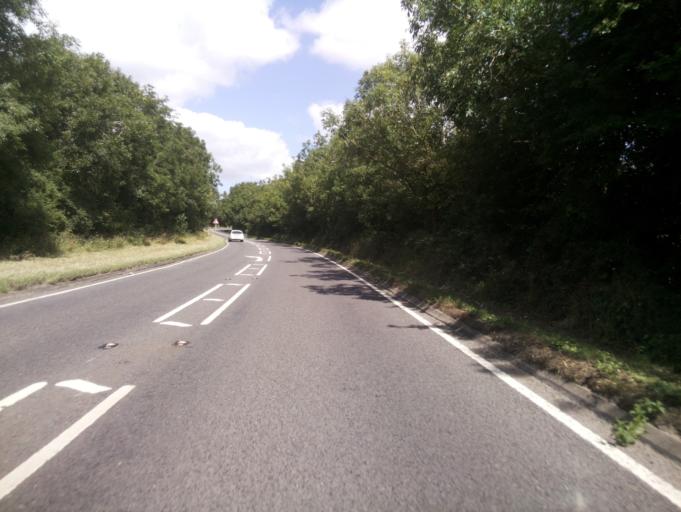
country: GB
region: England
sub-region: Buckinghamshire
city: Aylesbury
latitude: 51.8721
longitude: -0.8321
